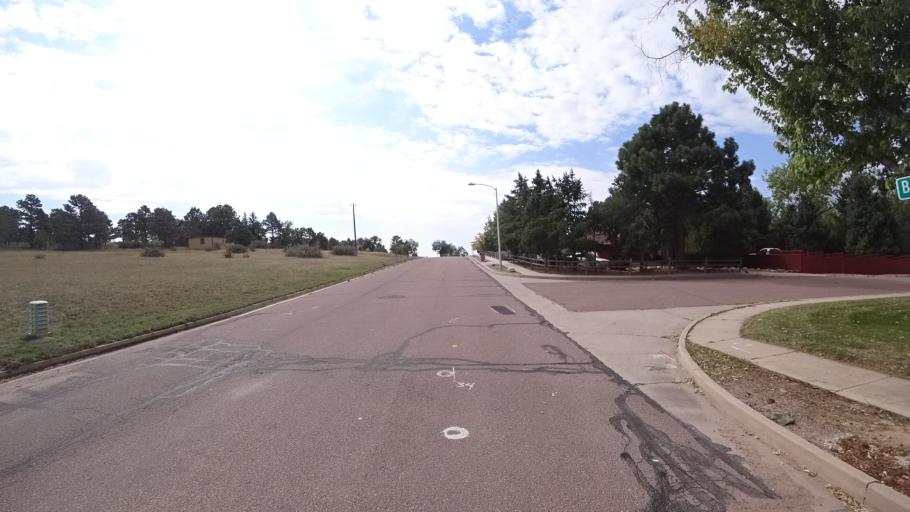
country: US
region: Colorado
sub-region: El Paso County
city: Cimarron Hills
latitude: 38.8538
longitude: -104.7273
